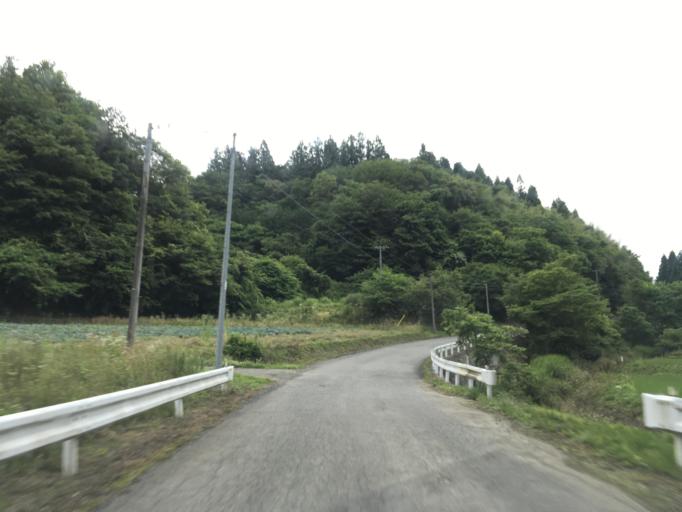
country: JP
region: Iwate
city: Ichinoseki
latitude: 38.8505
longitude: 141.3211
